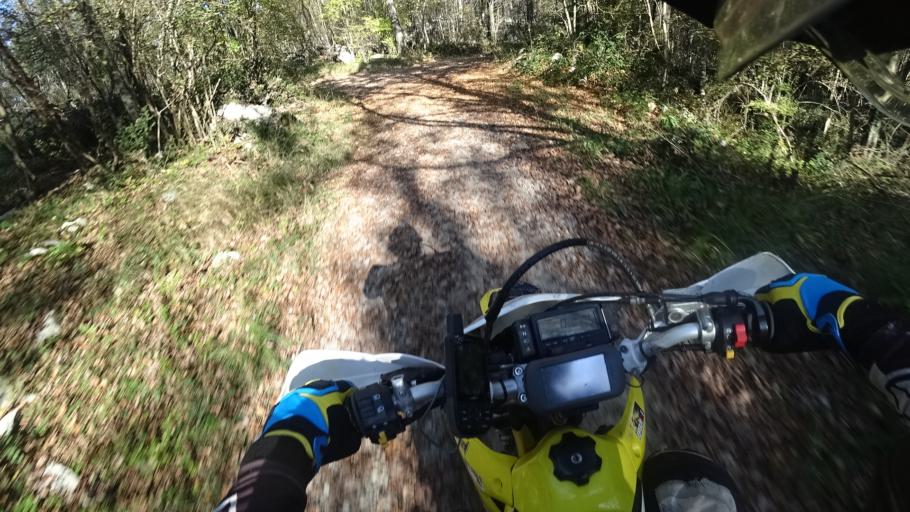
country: HR
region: Primorsko-Goranska
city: Kastav
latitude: 45.4027
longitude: 14.3311
